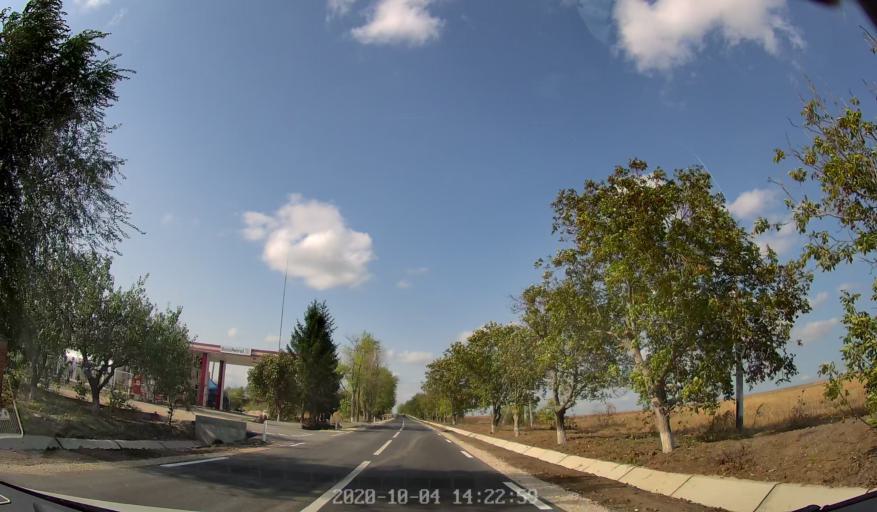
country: MD
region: Rezina
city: Saharna
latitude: 47.6042
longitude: 28.9421
